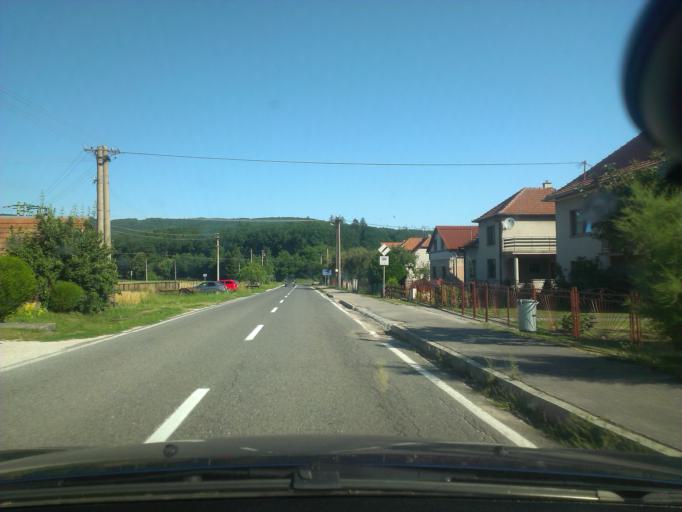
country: CZ
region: South Moravian
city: Velka nad Velickou
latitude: 48.8173
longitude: 17.5124
